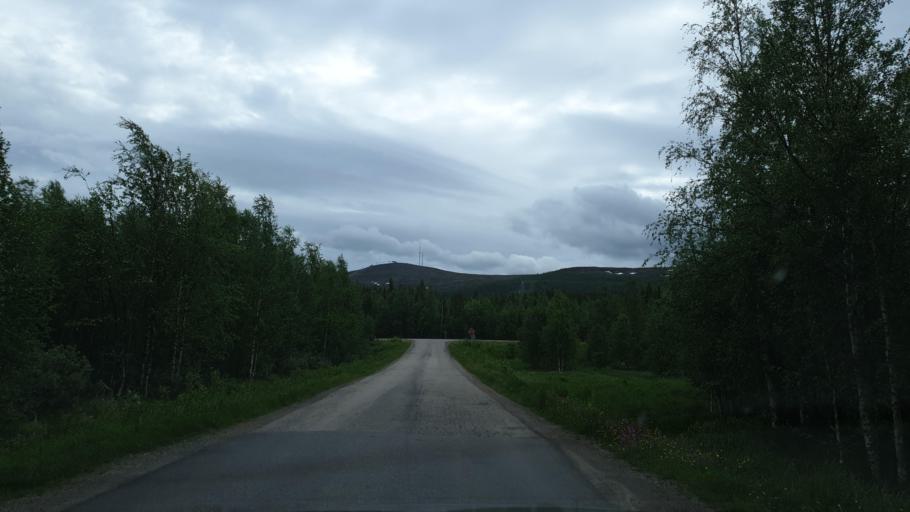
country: SE
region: Norrbotten
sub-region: Gallivare Kommun
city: Gaellivare
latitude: 67.1302
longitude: 20.6260
